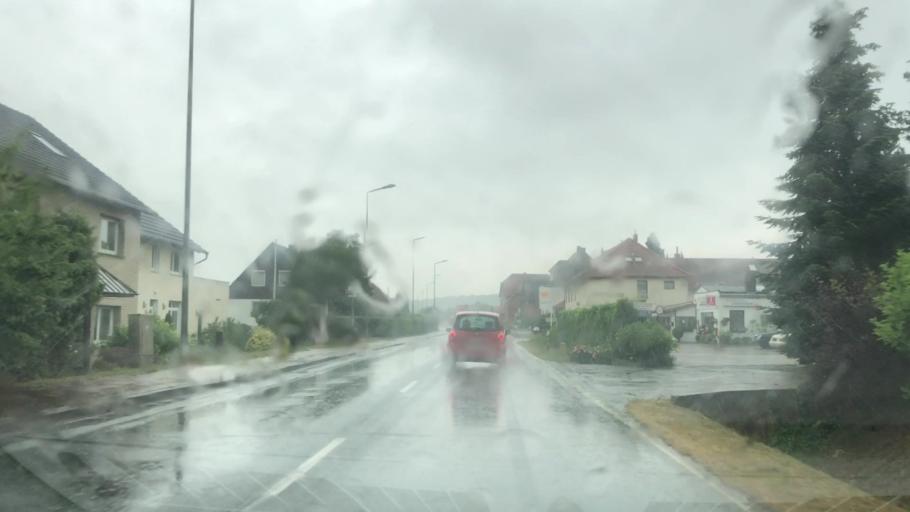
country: DE
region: North Rhine-Westphalia
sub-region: Regierungsbezirk Detmold
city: Minden
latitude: 52.2737
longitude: 8.9687
